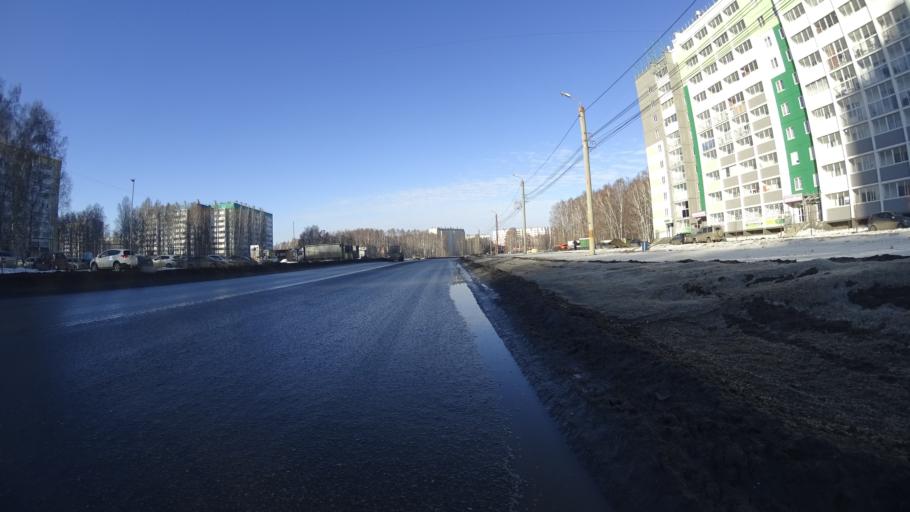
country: RU
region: Chelyabinsk
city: Roshchino
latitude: 55.2119
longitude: 61.2843
